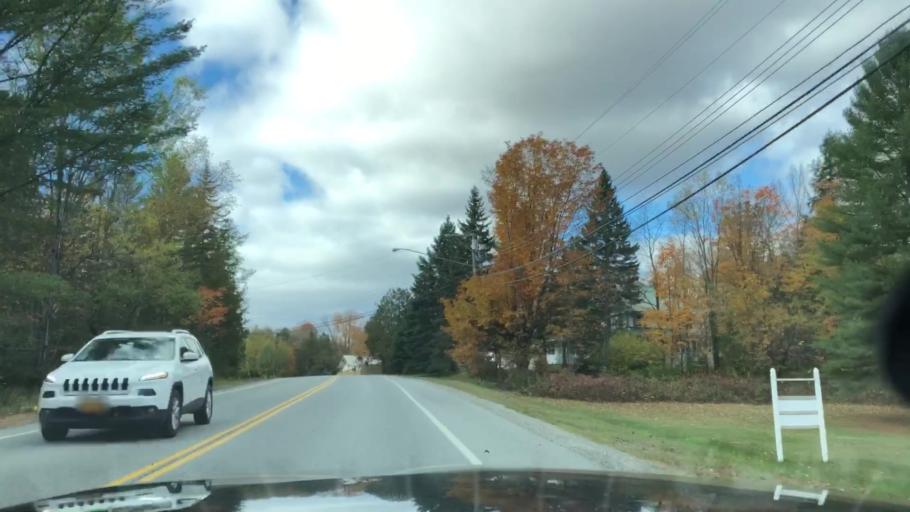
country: US
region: New York
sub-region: Essex County
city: Lake Placid
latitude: 43.9707
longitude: -74.1489
